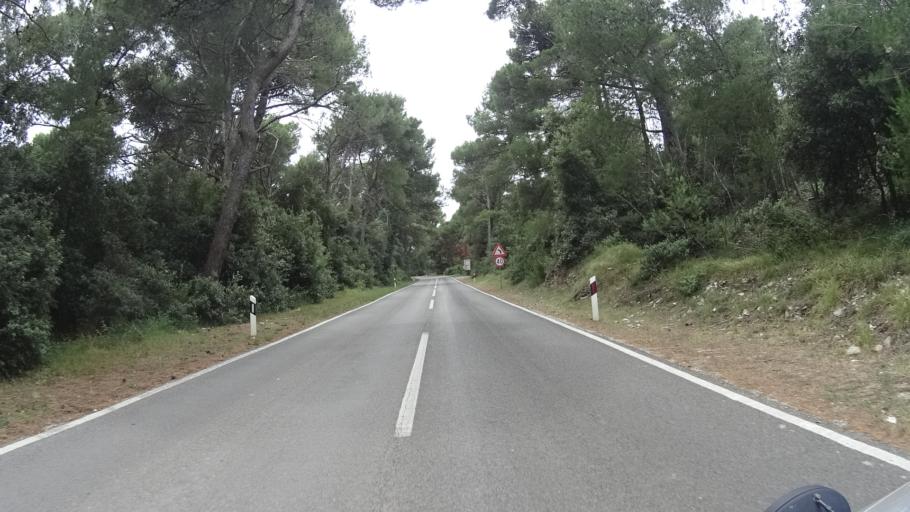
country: HR
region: Istarska
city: Medulin
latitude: 44.8112
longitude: 13.9098
